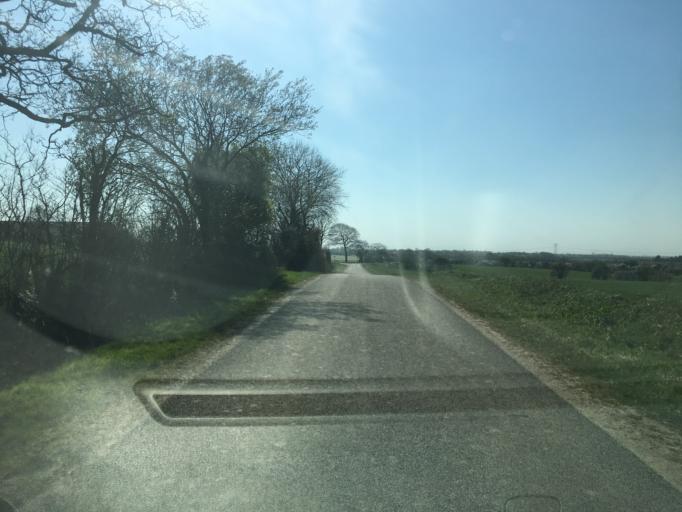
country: DK
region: South Denmark
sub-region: Aabenraa Kommune
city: Rodekro
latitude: 54.9980
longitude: 9.3226
